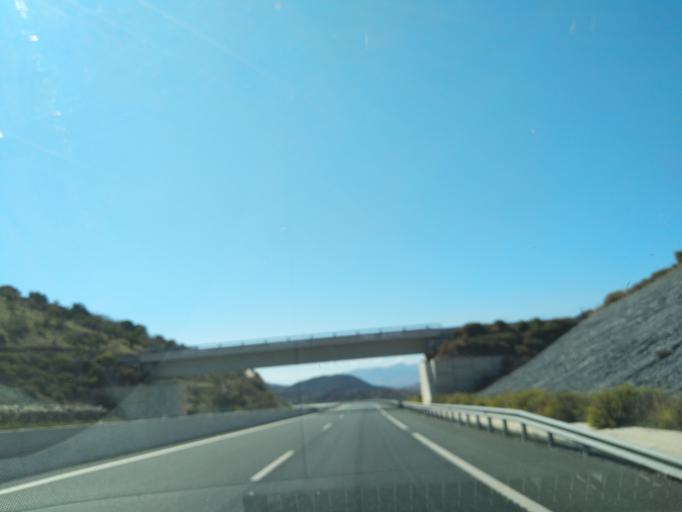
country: ES
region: Andalusia
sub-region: Provincia de Malaga
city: Almogia
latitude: 36.8125
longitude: -4.4705
